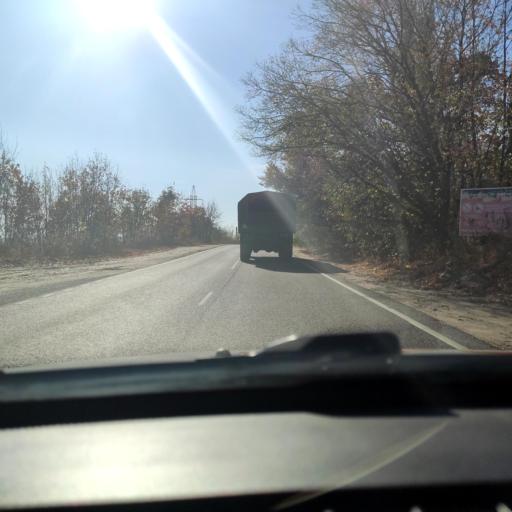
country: RU
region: Voronezj
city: Shilovo
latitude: 51.5629
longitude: 39.1401
